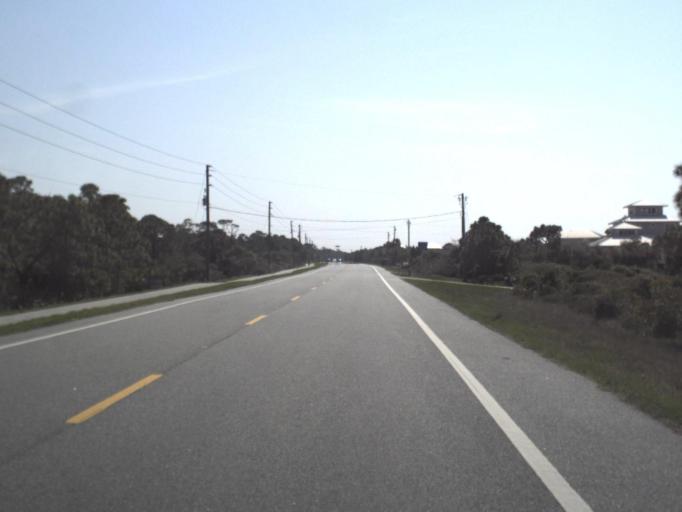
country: US
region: Florida
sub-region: Gulf County
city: Port Saint Joe
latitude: 29.7199
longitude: -85.3858
